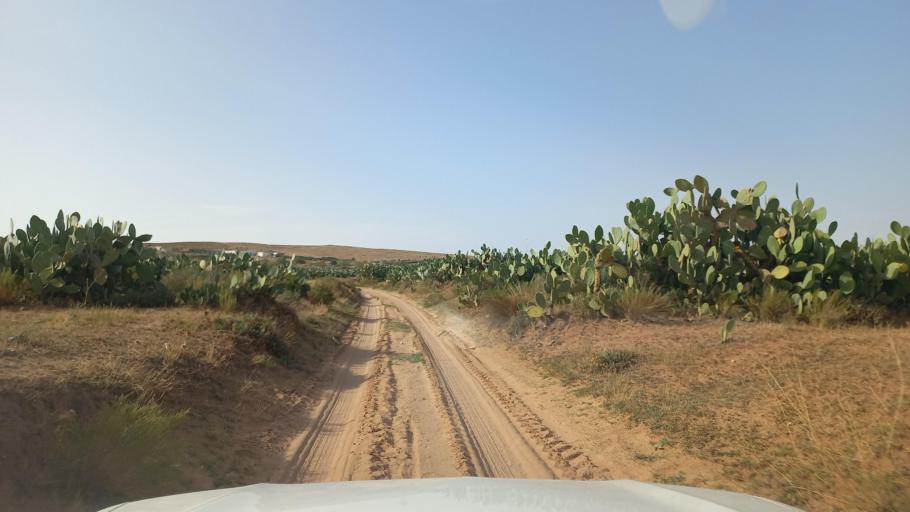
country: TN
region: Al Qasrayn
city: Kasserine
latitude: 35.3597
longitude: 8.8518
